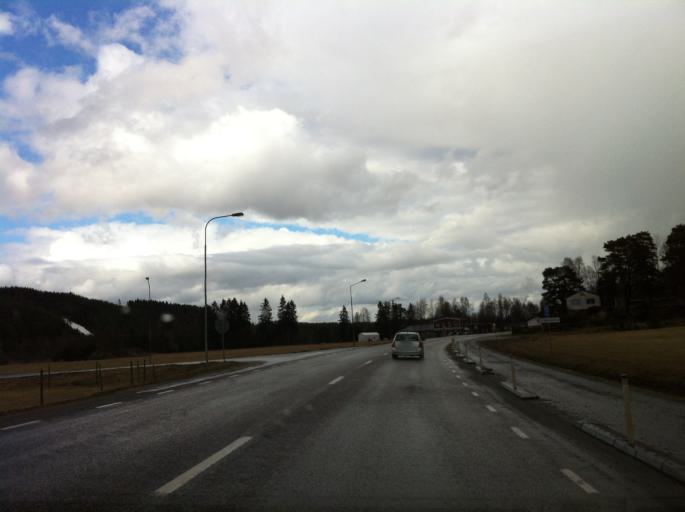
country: SE
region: Vaestra Goetaland
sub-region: Ulricehamns Kommun
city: Ulricehamn
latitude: 57.7462
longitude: 13.4242
